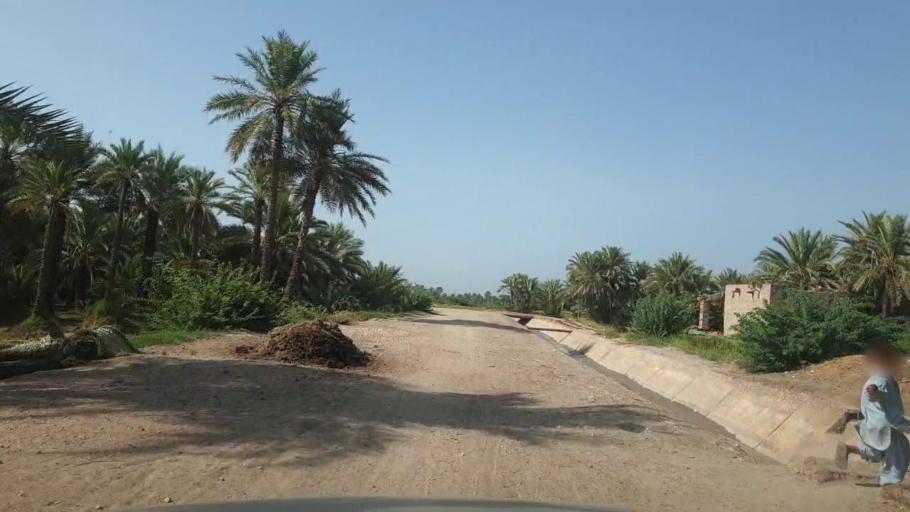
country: PK
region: Sindh
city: Rohri
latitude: 27.6594
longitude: 68.8840
